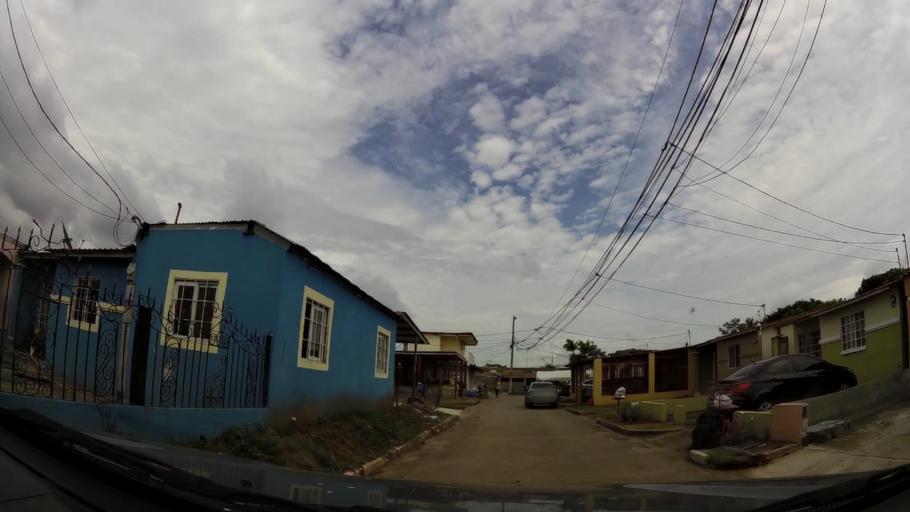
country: PA
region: Panama
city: Tocumen
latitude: 9.0404
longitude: -79.4079
